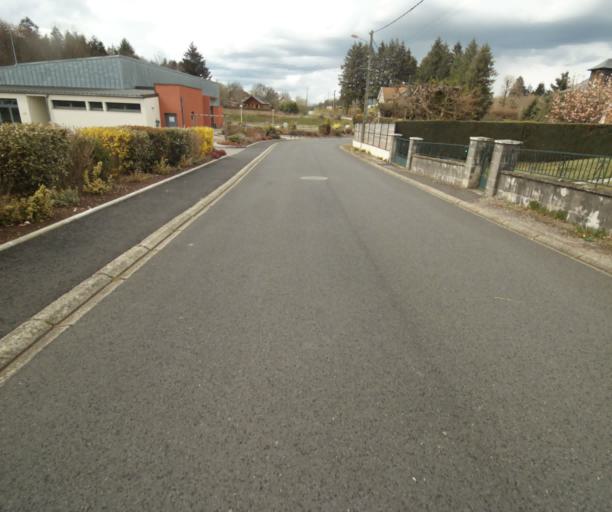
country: FR
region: Limousin
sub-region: Departement de la Correze
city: Correze
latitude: 45.3345
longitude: 1.9425
